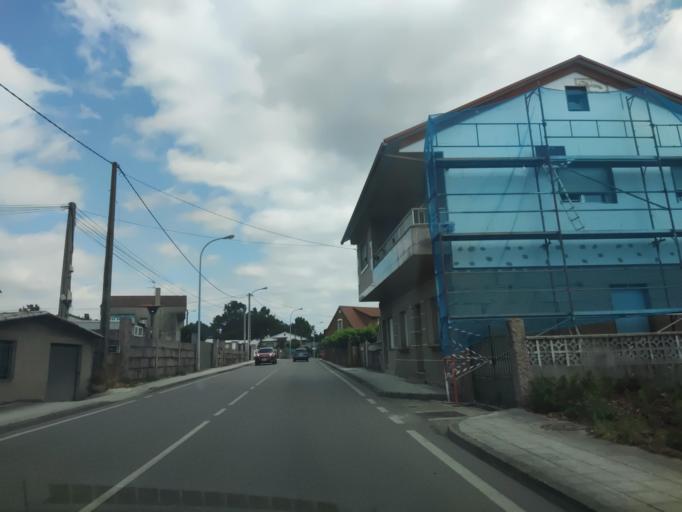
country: ES
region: Galicia
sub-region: Provincia de Pontevedra
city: Porrino
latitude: 42.1577
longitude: -8.6282
